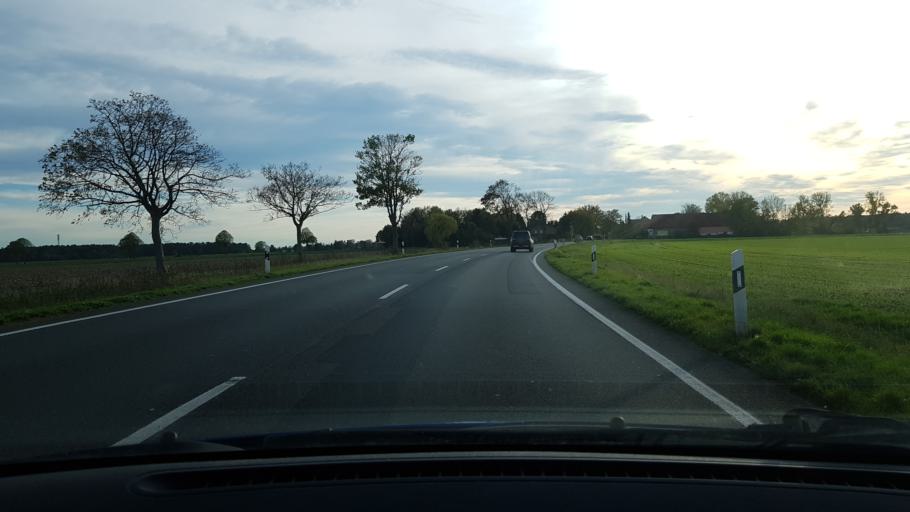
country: DE
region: Lower Saxony
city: Rotgesbuttel
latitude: 52.4350
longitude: 10.5372
